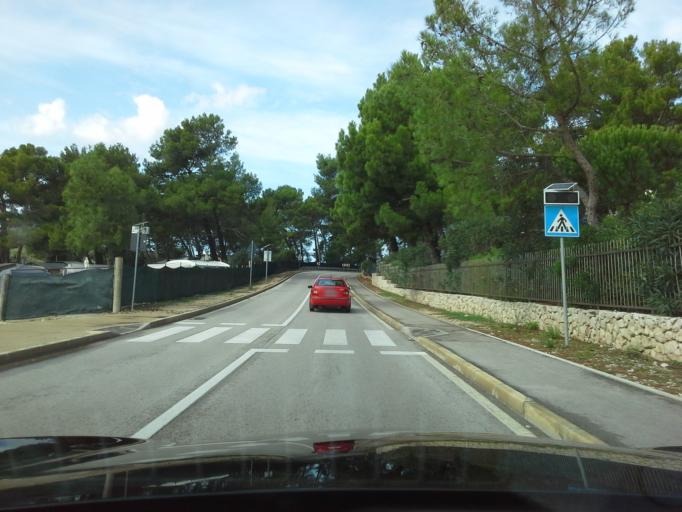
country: HR
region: Primorsko-Goranska
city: Mali Losinj
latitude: 44.5538
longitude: 14.4444
